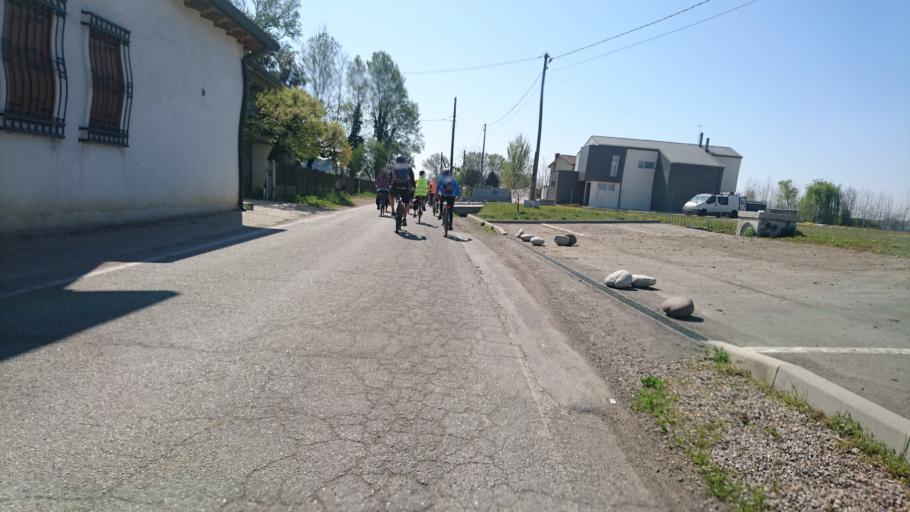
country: IT
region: Veneto
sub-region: Provincia di Padova
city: Cittadella
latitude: 45.6231
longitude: 11.7800
